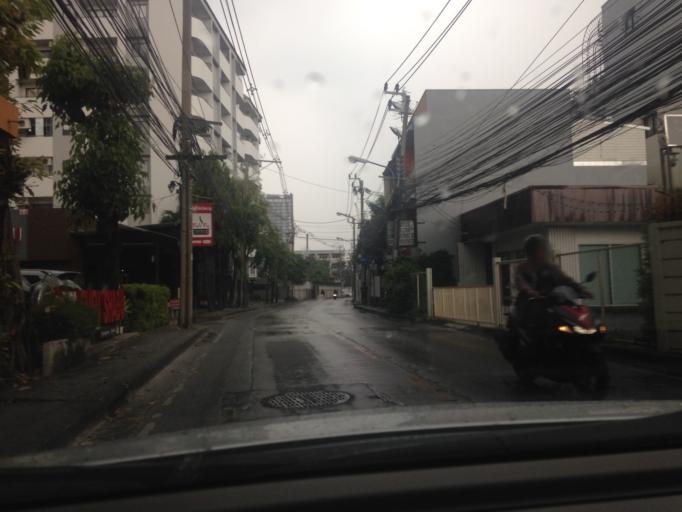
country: TH
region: Bangkok
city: Phaya Thai
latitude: 13.7788
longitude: 100.5383
